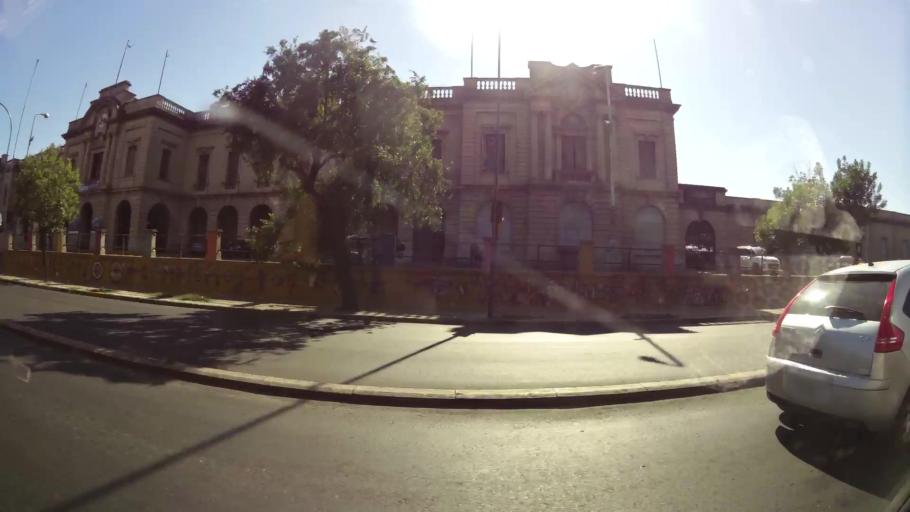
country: AR
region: Cordoba
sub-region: Departamento de Capital
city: Cordoba
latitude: -31.4209
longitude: -64.1754
